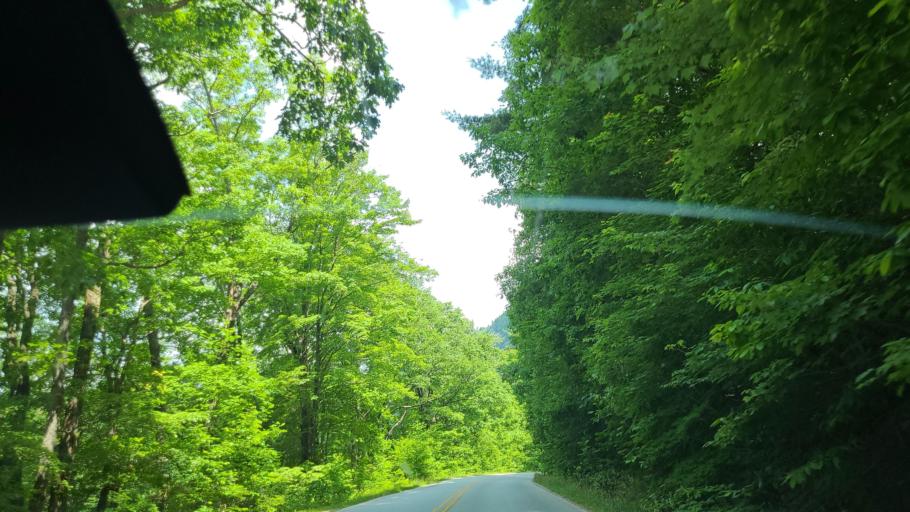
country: US
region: Georgia
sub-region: Rabun County
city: Mountain City
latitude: 35.0205
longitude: -83.1869
